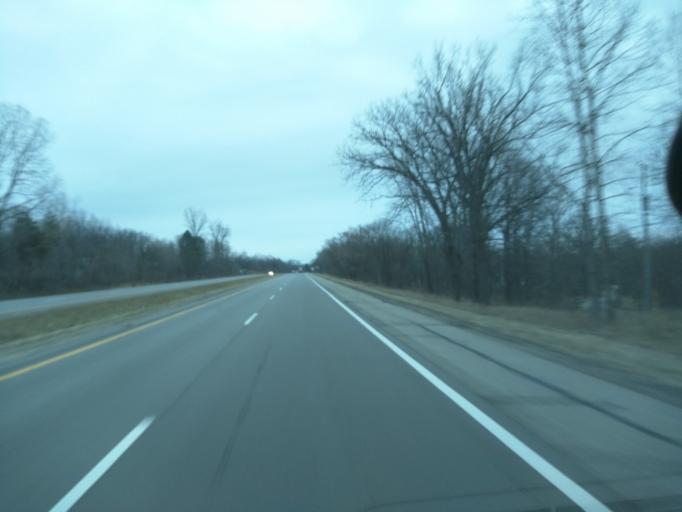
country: US
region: Michigan
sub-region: Ingham County
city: Leslie
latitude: 42.4243
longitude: -84.4353
